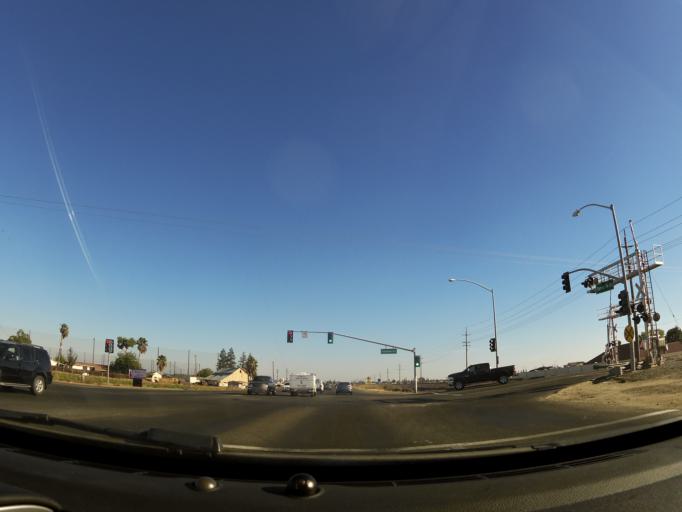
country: US
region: California
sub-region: Merced County
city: Atwater
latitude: 37.3404
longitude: -120.5408
